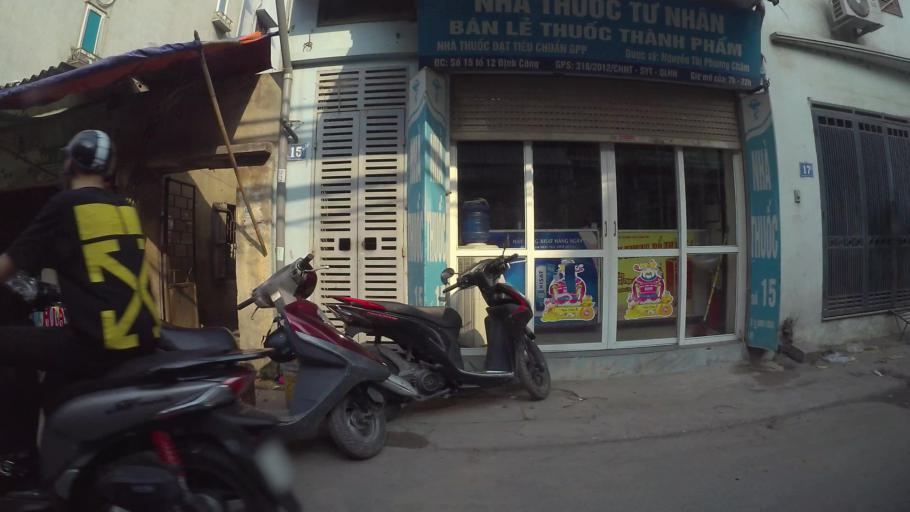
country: VN
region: Ha Noi
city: Thanh Xuan
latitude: 20.9806
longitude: 105.8268
